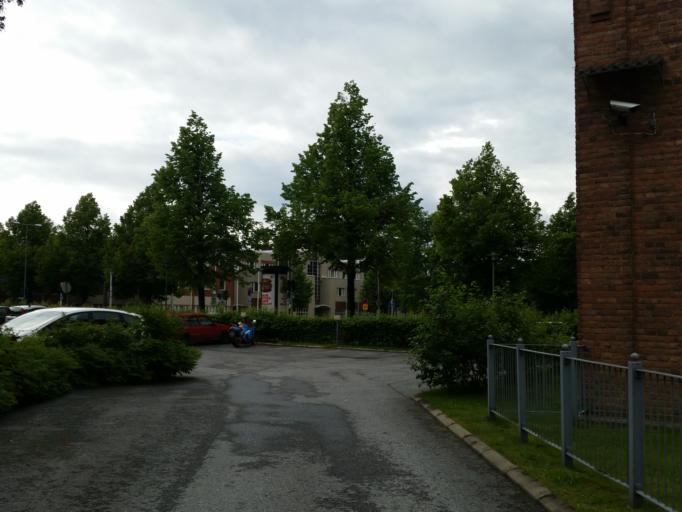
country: FI
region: Northern Savo
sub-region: Kuopio
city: Kuopio
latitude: 62.8950
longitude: 27.6717
